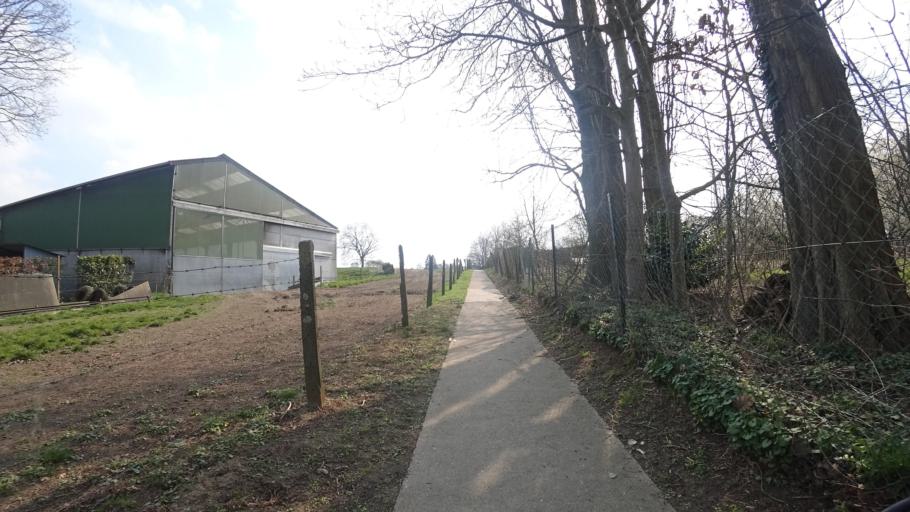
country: BE
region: Wallonia
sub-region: Province du Brabant Wallon
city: Chastre-Villeroux-Blanmont
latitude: 50.6223
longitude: 4.6428
